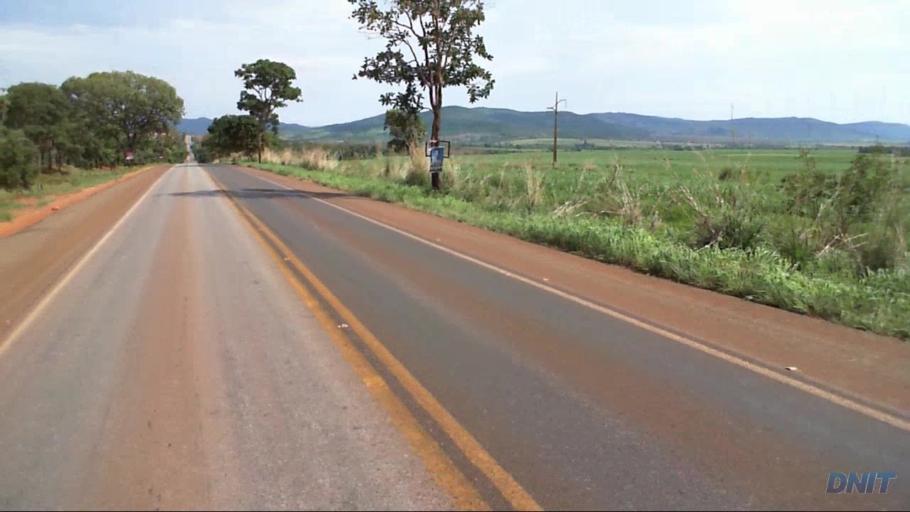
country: BR
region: Goias
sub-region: Barro Alto
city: Barro Alto
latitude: -15.0209
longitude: -48.8973
